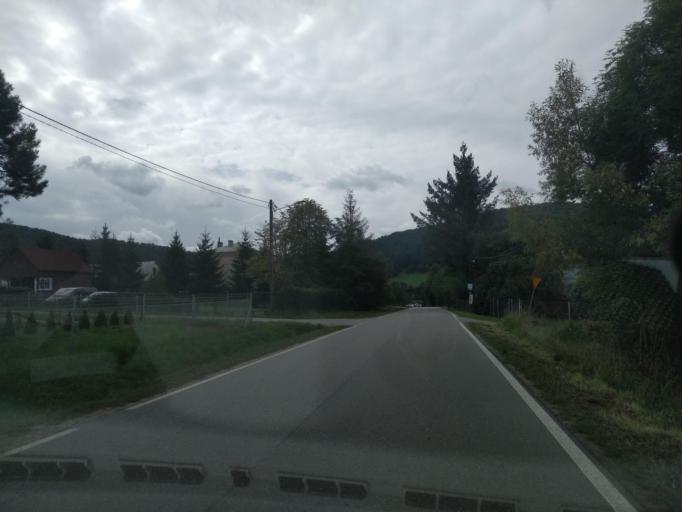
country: PL
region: Lesser Poland Voivodeship
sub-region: Powiat gorlicki
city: Ropa
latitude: 49.5746
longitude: 21.0944
